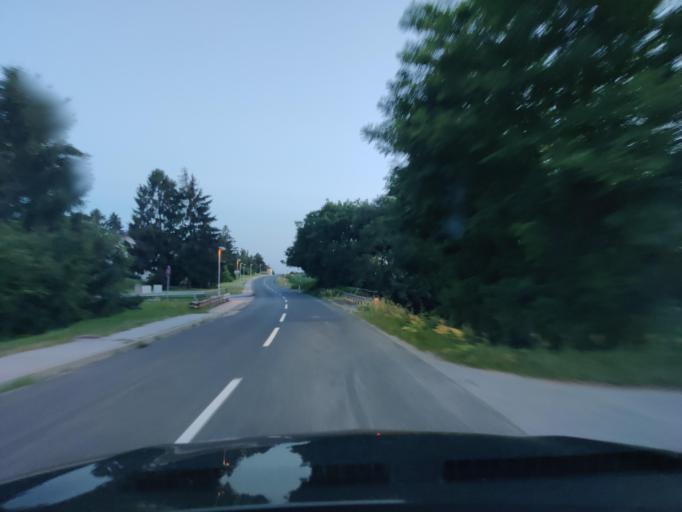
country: SI
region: Lendava-Lendva
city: Lendava
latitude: 46.5883
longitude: 16.4523
